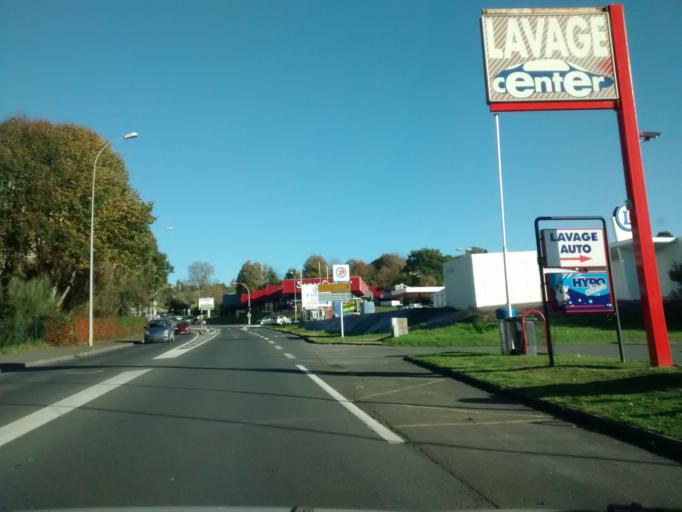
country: FR
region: Brittany
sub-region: Departement des Cotes-d'Armor
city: Lannion
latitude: 48.7261
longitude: -3.4500
